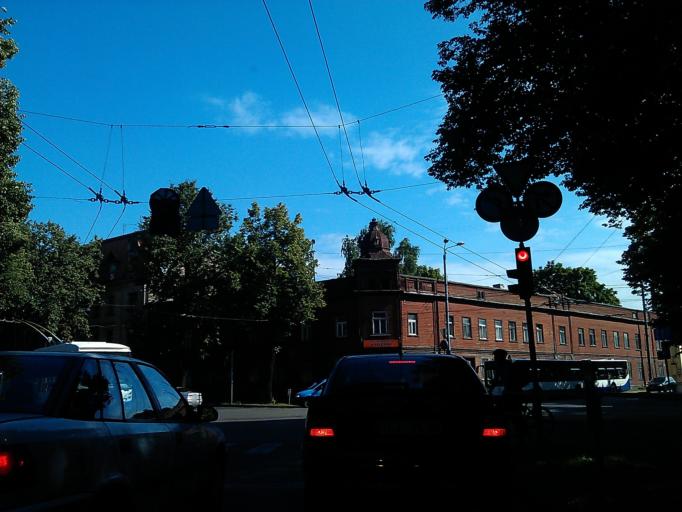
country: LV
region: Riga
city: Riga
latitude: 56.9541
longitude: 24.1515
